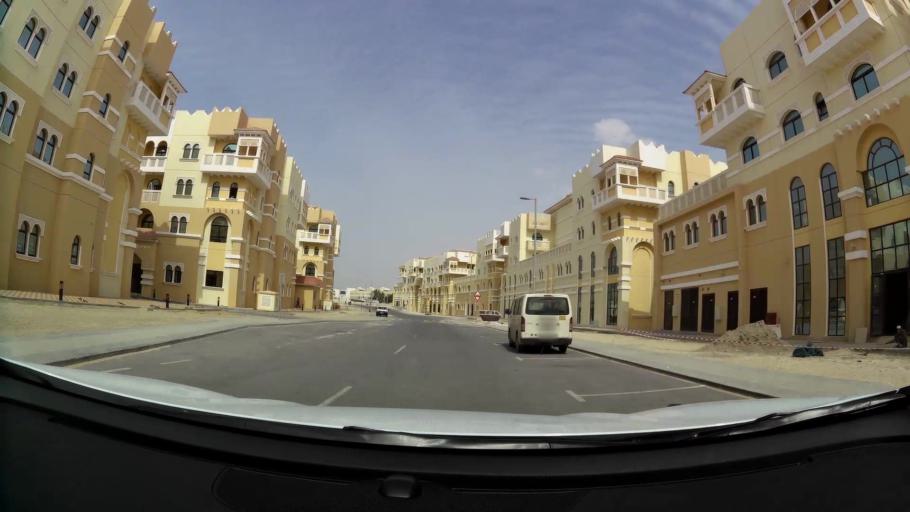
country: AE
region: Abu Dhabi
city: Abu Dhabi
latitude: 24.5504
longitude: 54.6919
